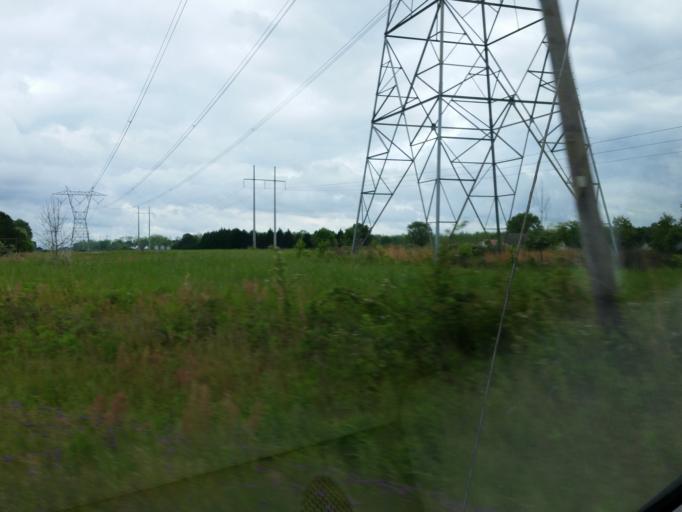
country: US
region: Georgia
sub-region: Peach County
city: Byron
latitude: 32.6517
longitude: -83.7853
